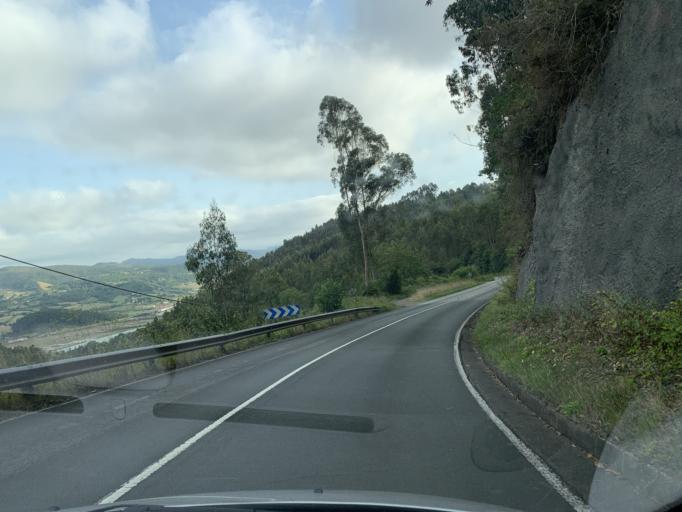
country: ES
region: Asturias
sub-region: Province of Asturias
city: Villaviciosa
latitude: 43.5157
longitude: -5.4266
